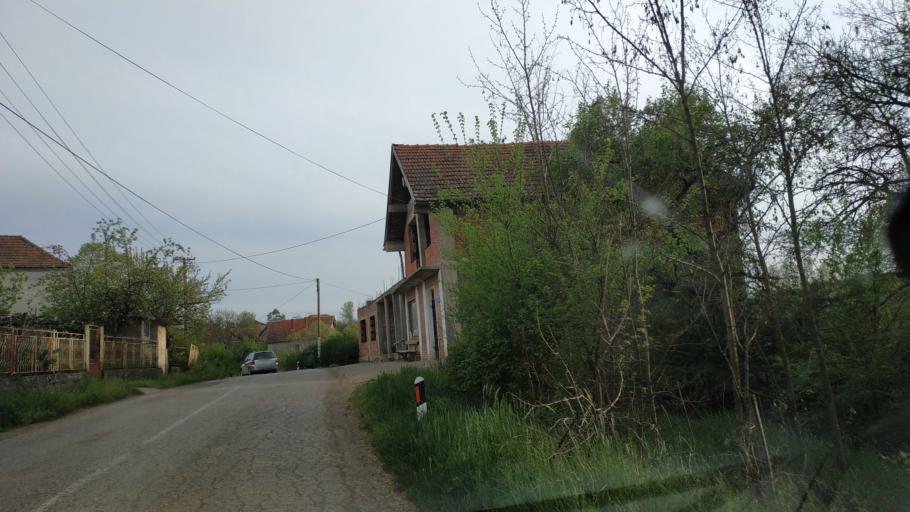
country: RS
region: Central Serbia
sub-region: Nisavski Okrug
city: Aleksinac
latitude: 43.4850
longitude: 21.8179
